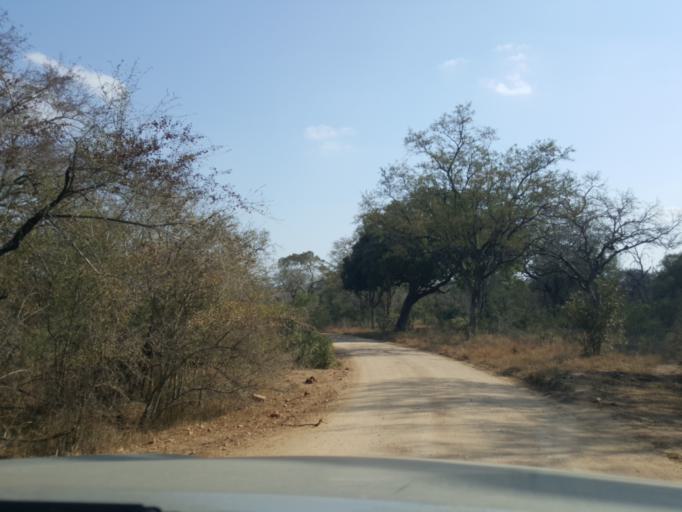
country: ZA
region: Mpumalanga
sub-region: Ehlanzeni District
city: Komatipoort
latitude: -25.2907
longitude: 31.7650
